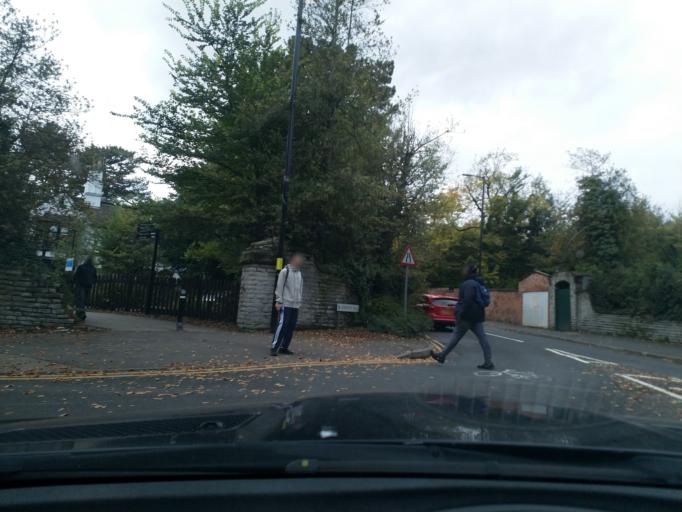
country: GB
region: England
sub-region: City and Borough of Birmingham
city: Birmingham
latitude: 52.4576
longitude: -1.9269
